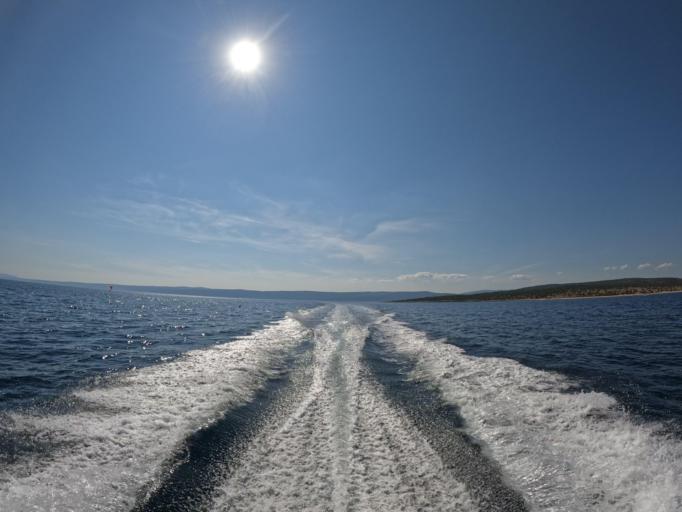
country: HR
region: Primorsko-Goranska
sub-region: Grad Krk
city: Krk
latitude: 44.9523
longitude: 14.5576
